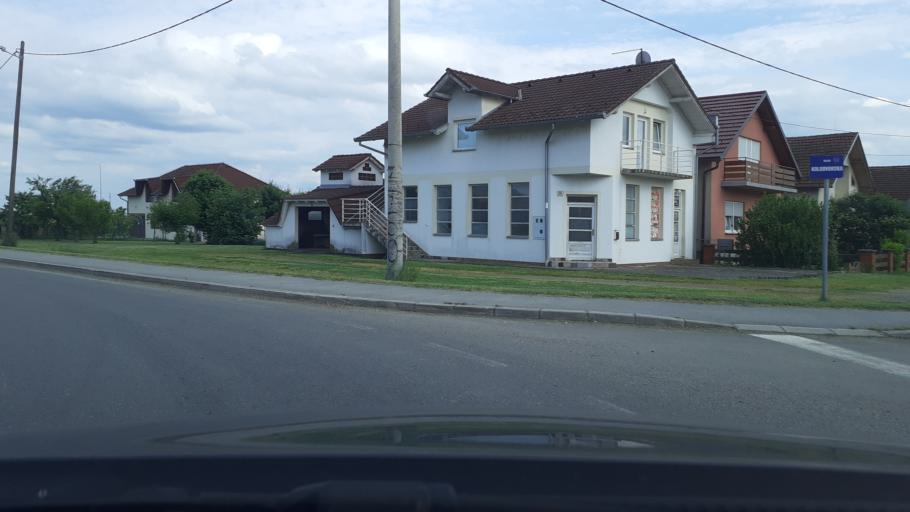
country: HR
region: Brodsko-Posavska
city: Slobodnica
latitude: 45.1729
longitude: 17.9285
